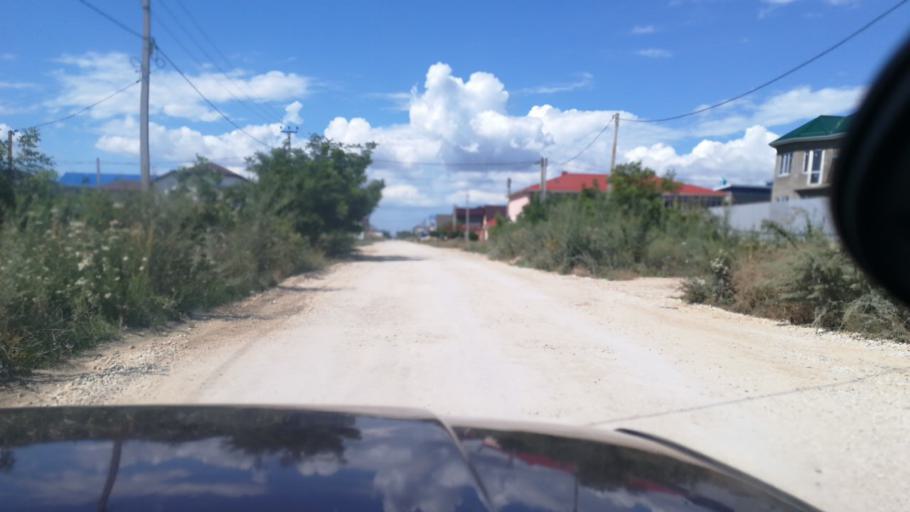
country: RU
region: Krasnodarskiy
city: Vityazevo
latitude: 45.0032
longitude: 37.2969
